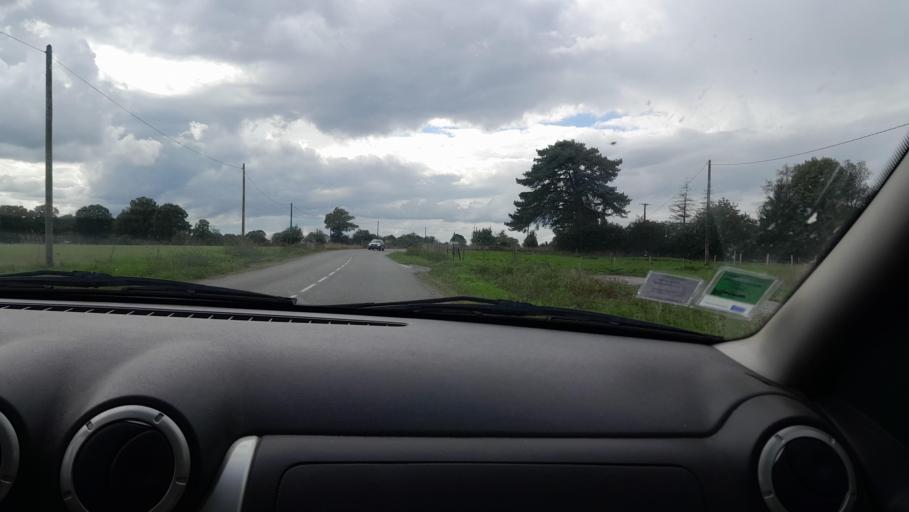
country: FR
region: Brittany
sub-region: Departement d'Ille-et-Vilaine
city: Le Pertre
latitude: 48.0383
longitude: -1.0501
